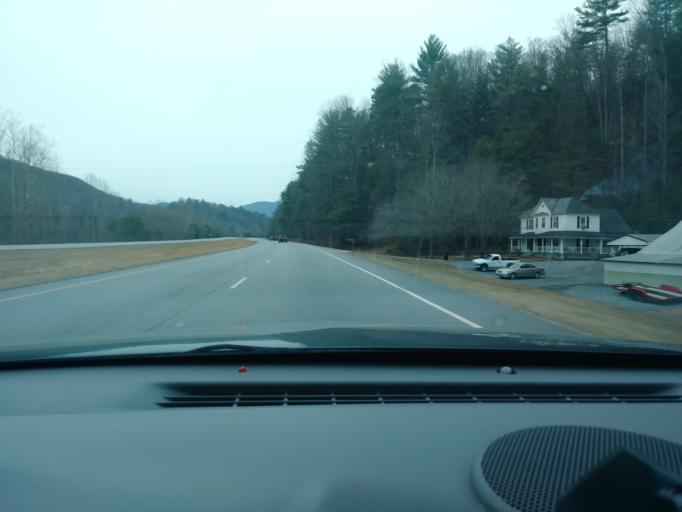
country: US
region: North Carolina
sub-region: Wilkes County
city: Millers Creek
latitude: 36.1841
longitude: -81.4012
